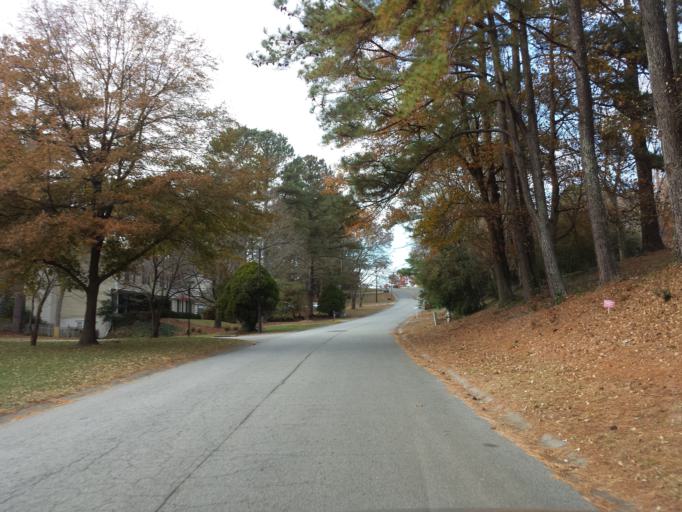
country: US
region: Georgia
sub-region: Fulton County
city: Sandy Springs
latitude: 33.9593
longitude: -84.4290
